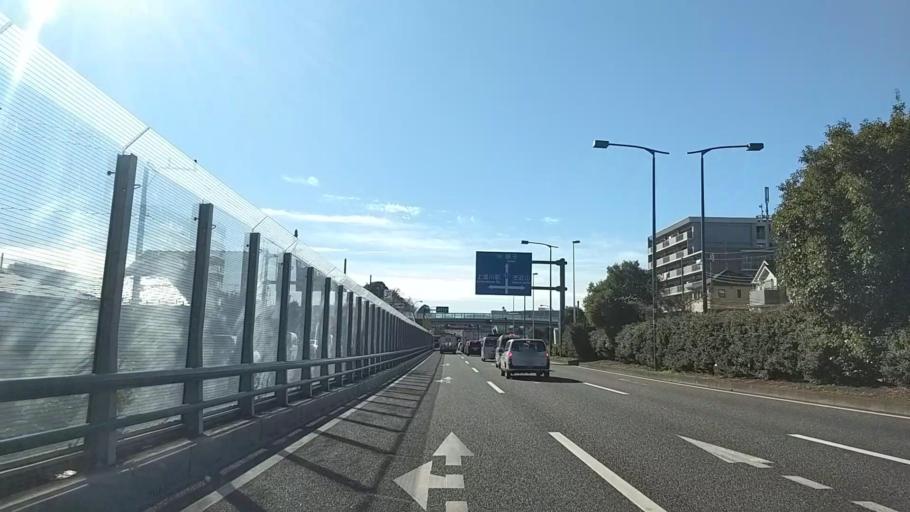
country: JP
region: Kanagawa
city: Yokohama
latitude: 35.4649
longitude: 139.5647
